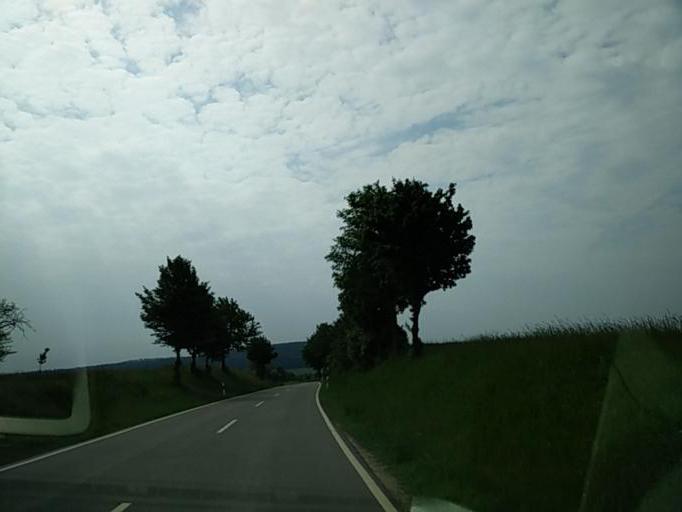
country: DE
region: Baden-Wuerttemberg
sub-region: Tuebingen Region
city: Hirrlingen
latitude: 48.4205
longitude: 8.8834
